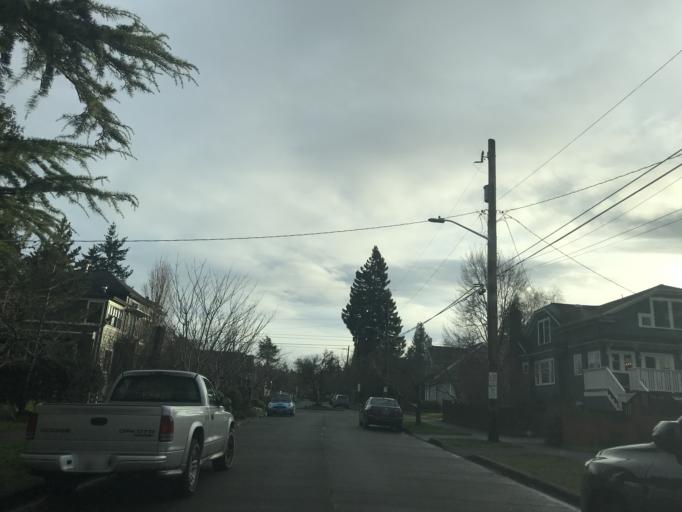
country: US
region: Washington
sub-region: King County
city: Seattle
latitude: 47.6416
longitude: -122.3004
